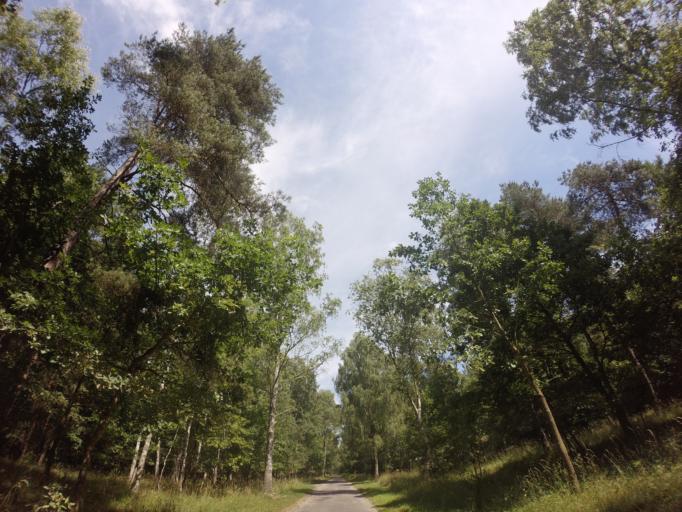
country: PL
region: West Pomeranian Voivodeship
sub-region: Powiat choszczenski
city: Recz
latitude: 53.3367
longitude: 15.5211
